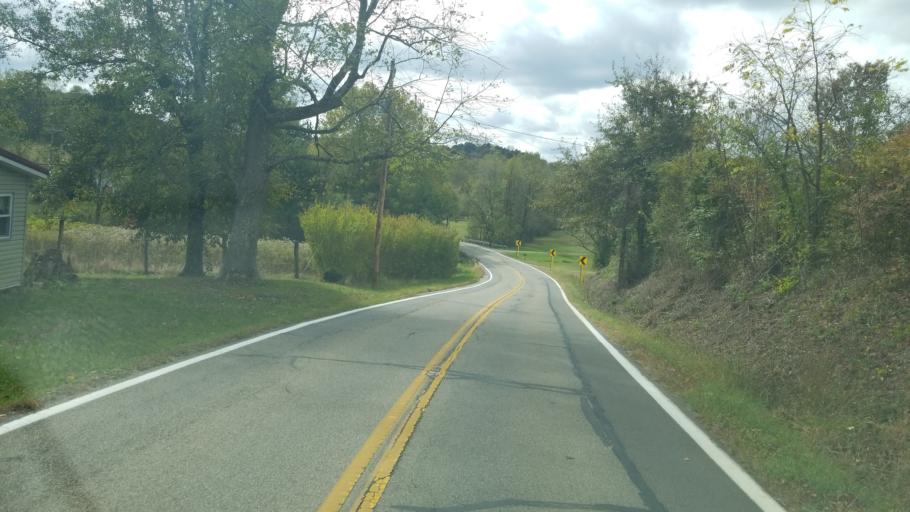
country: US
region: Ohio
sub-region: Jackson County
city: Wellston
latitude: 39.1009
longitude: -82.5769
